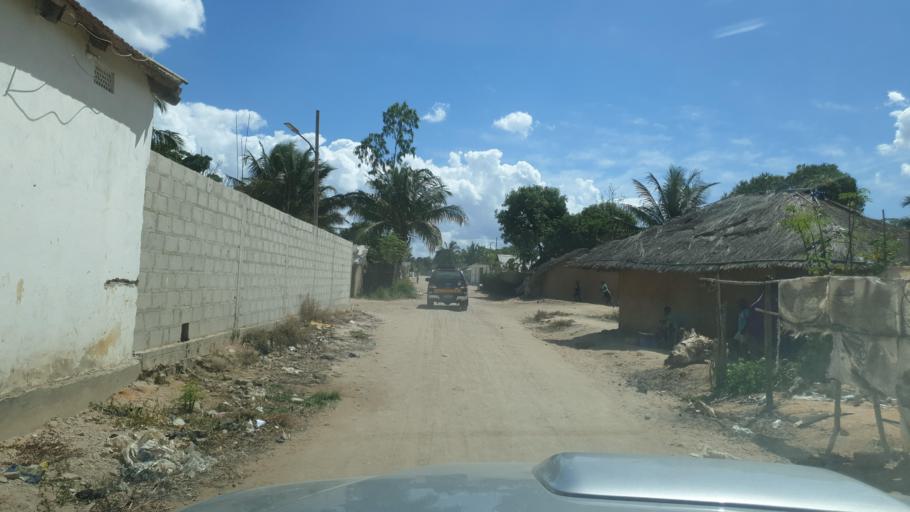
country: MZ
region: Nampula
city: Nacala
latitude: -14.5732
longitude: 40.6913
